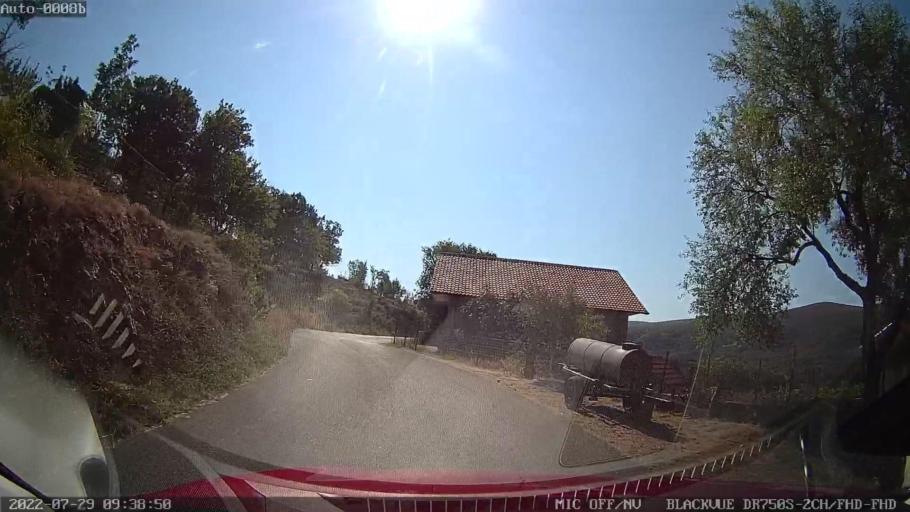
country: HR
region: Zadarska
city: Obrovac
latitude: 44.1964
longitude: 15.7519
